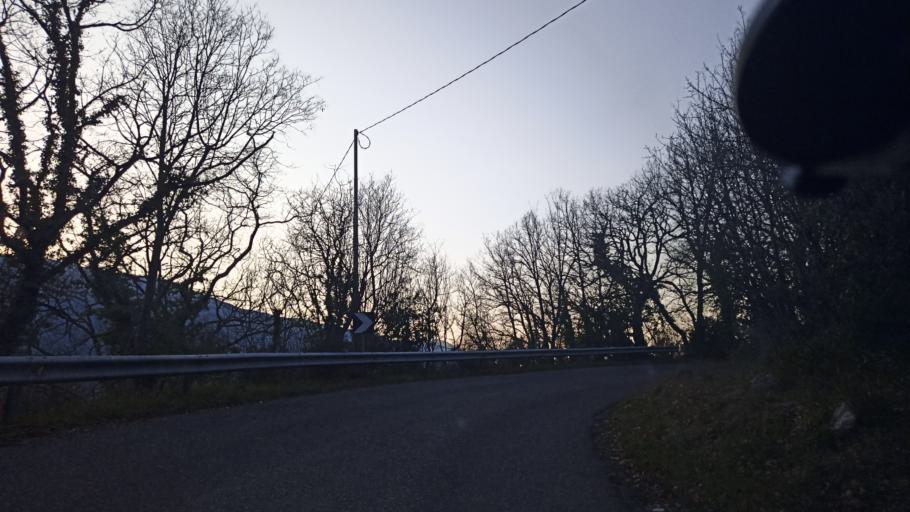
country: IT
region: Latium
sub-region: Provincia di Rieti
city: Cottanello
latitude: 42.4085
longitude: 12.6814
